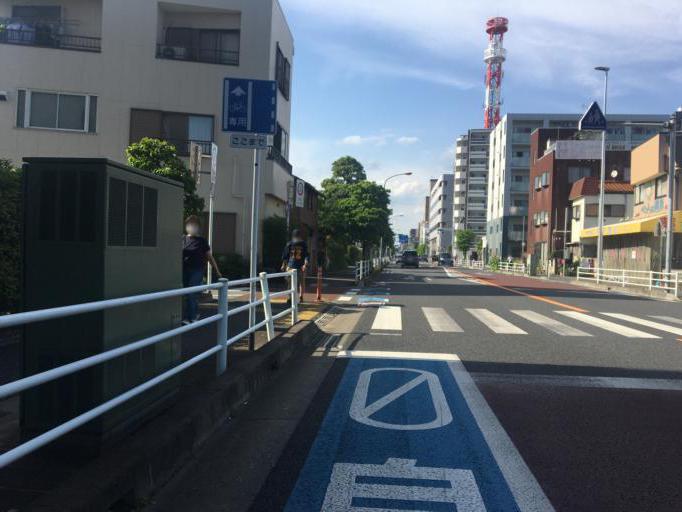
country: JP
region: Saitama
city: Yono
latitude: 35.8531
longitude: 139.6477
